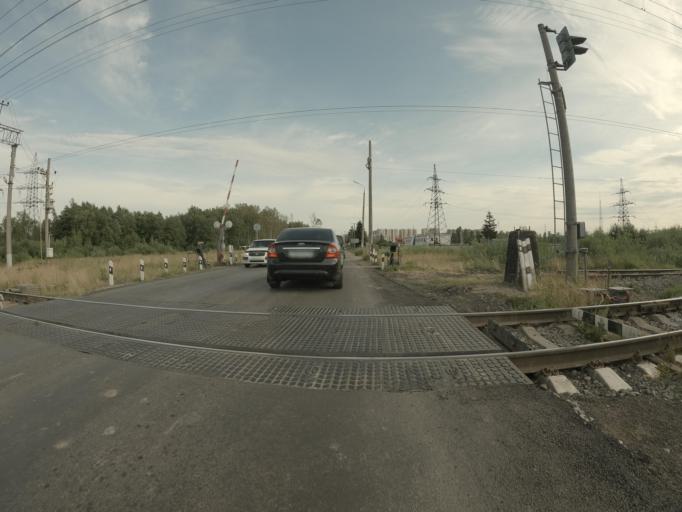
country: RU
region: St.-Petersburg
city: Krasnogvargeisky
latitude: 59.9319
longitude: 30.5203
